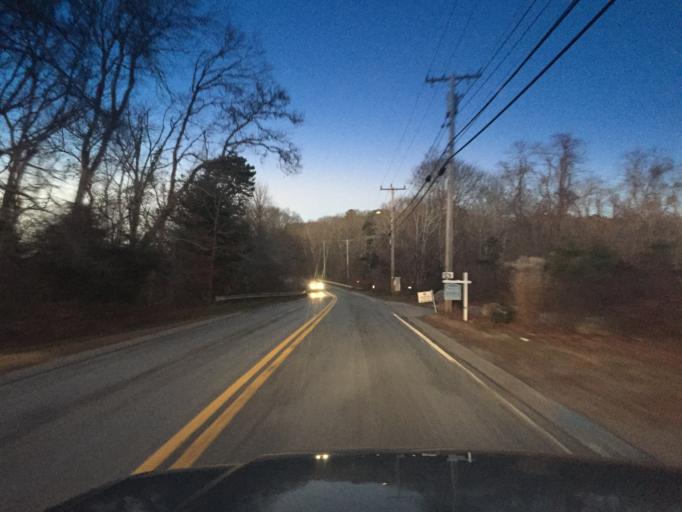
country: US
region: Massachusetts
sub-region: Barnstable County
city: West Falmouth
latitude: 41.6205
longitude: -70.6227
